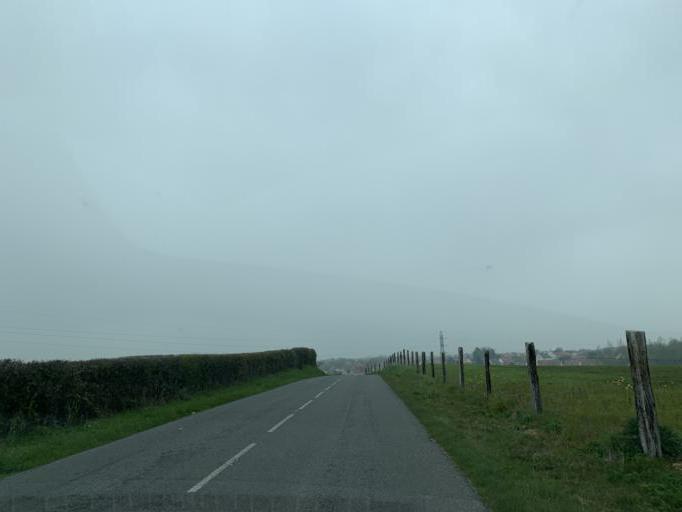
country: FR
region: Nord-Pas-de-Calais
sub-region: Departement du Pas-de-Calais
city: Marquise
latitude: 50.8053
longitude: 1.7113
